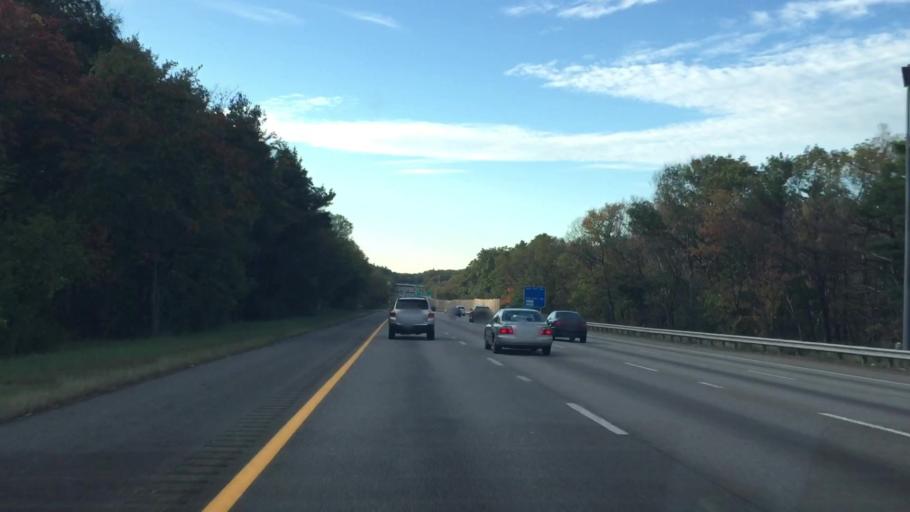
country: US
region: Massachusetts
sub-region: Norfolk County
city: Dedham
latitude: 42.2361
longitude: -71.1913
